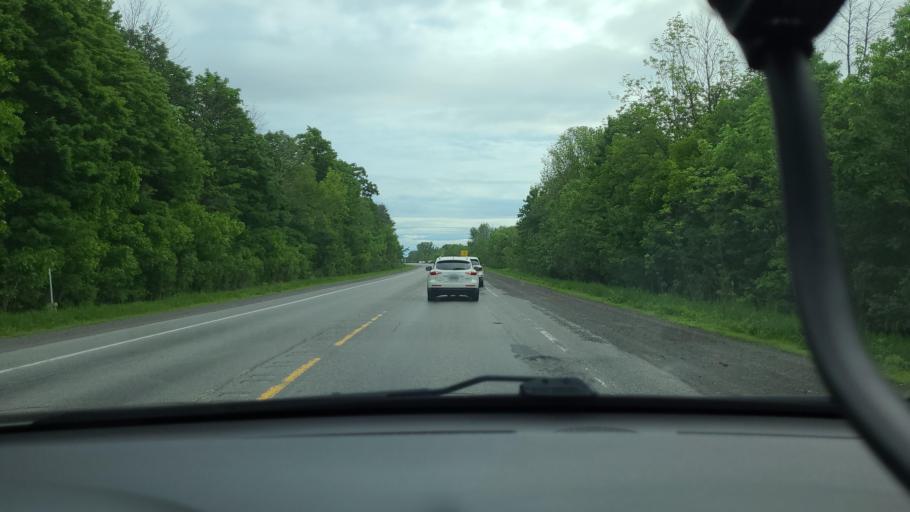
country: CA
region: Quebec
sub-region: Lanaudiere
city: Saint-Jacques
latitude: 45.9612
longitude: -73.5658
